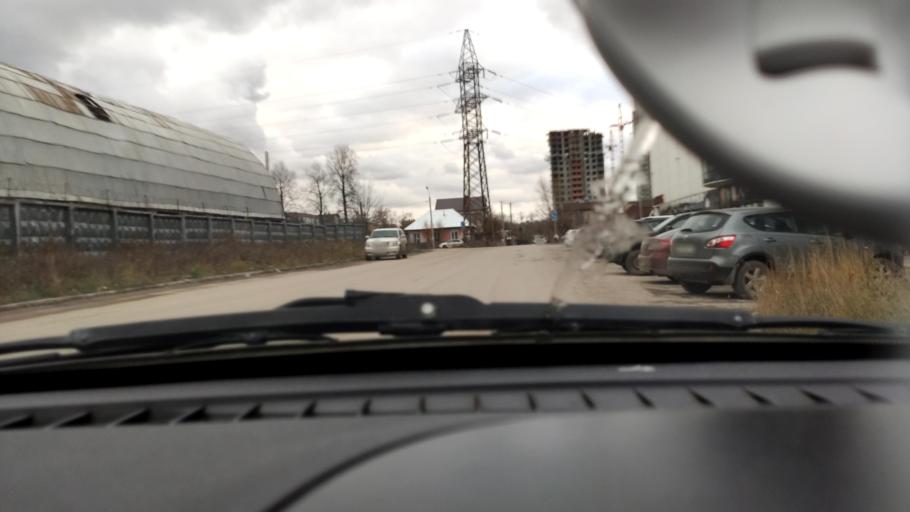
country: RU
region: Perm
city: Perm
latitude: 57.9769
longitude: 56.1907
